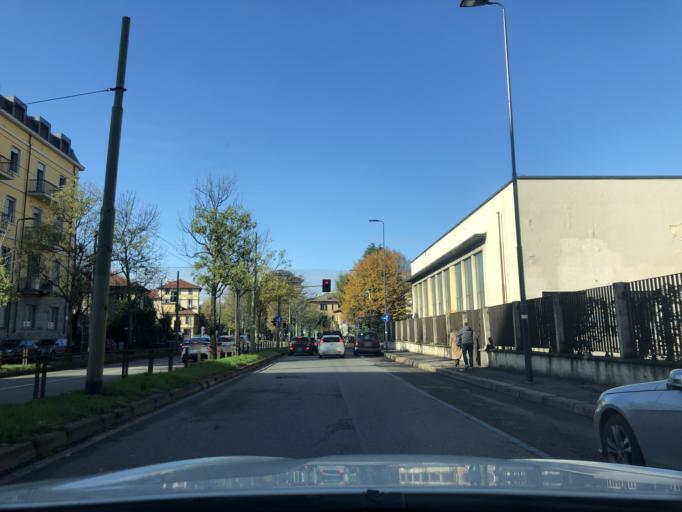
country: IT
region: Lombardy
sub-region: Citta metropolitana di Milano
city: Milano
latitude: 45.4905
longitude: 9.1996
